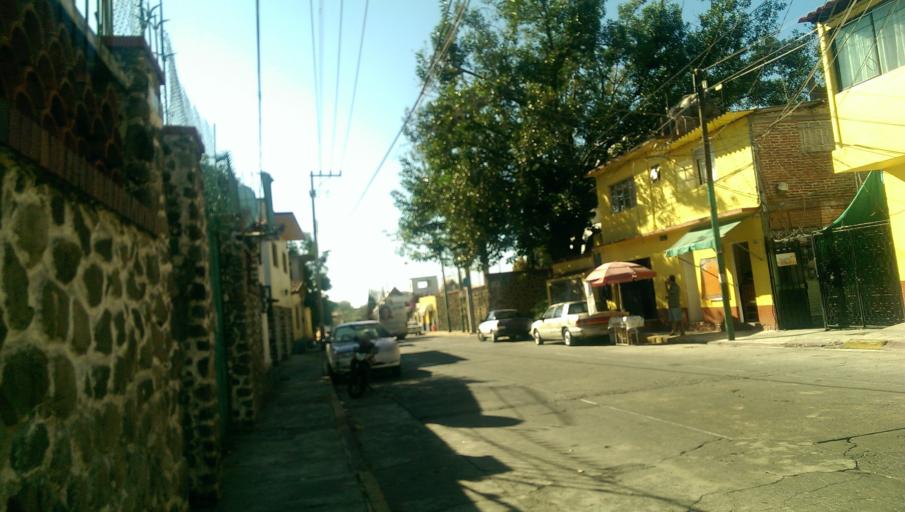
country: MX
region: Morelos
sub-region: Cuernavaca
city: Cuernavaca
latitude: 18.9206
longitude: -99.2415
